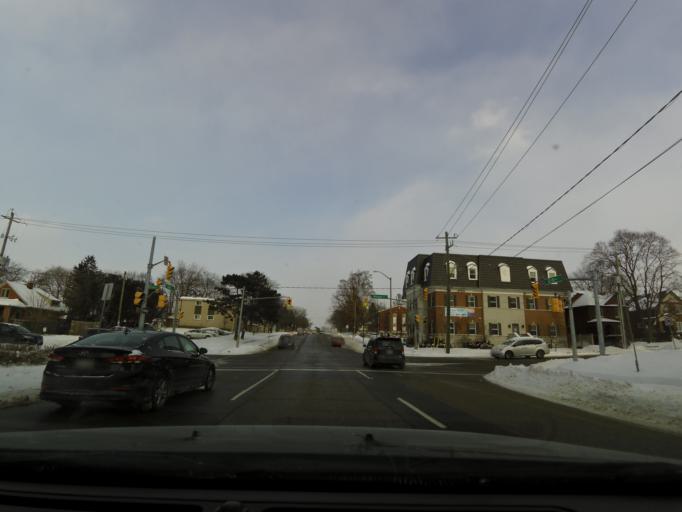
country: CA
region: Ontario
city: Waterloo
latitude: 43.4666
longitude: -80.5155
